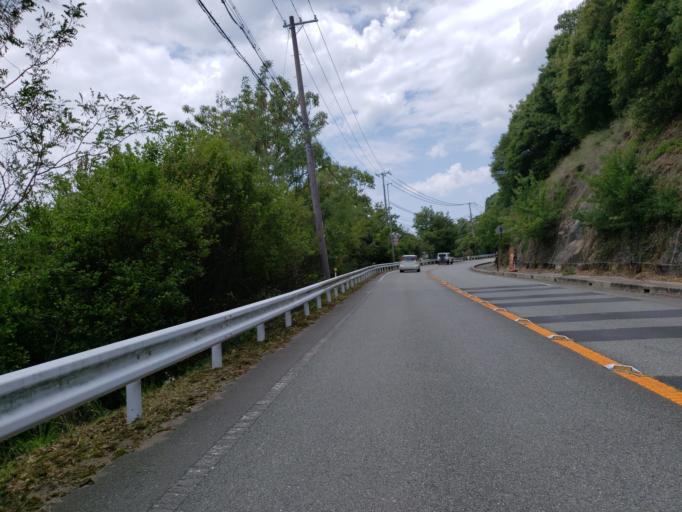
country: JP
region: Hyogo
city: Aioi
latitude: 34.7706
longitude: 134.5149
